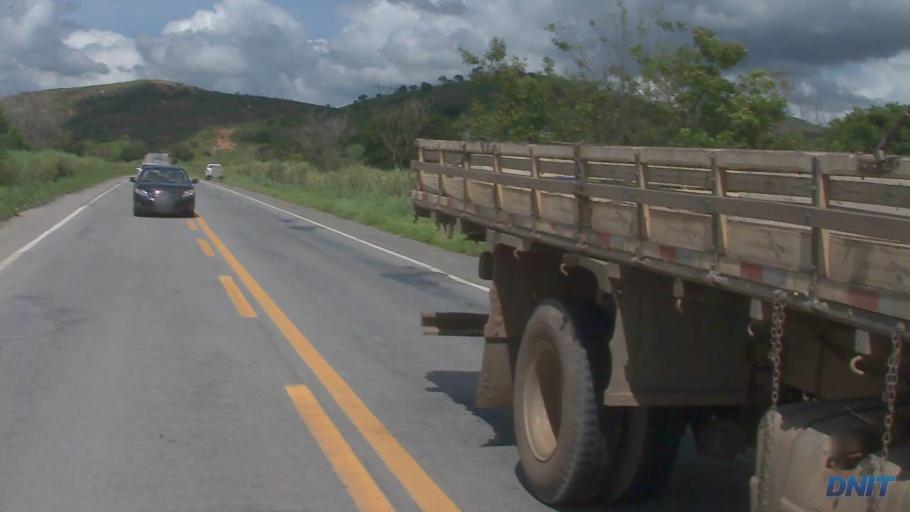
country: BR
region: Minas Gerais
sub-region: Governador Valadares
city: Governador Valadares
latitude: -19.0170
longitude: -42.1415
